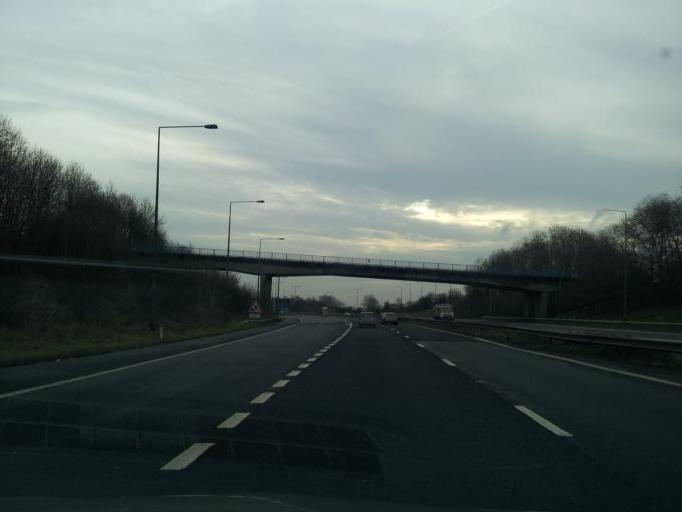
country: GB
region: England
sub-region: Borough of Rochdale
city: Rochdale
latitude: 53.5791
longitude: -2.1597
